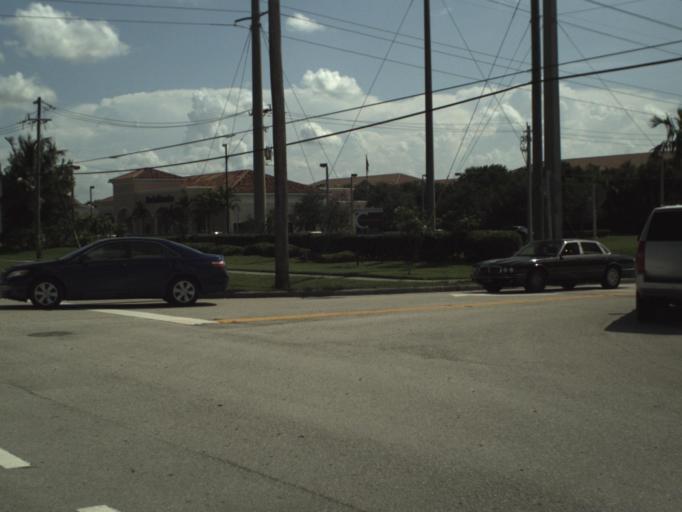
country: US
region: Florida
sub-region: Palm Beach County
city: Wellington
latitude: 26.6750
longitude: -80.2027
